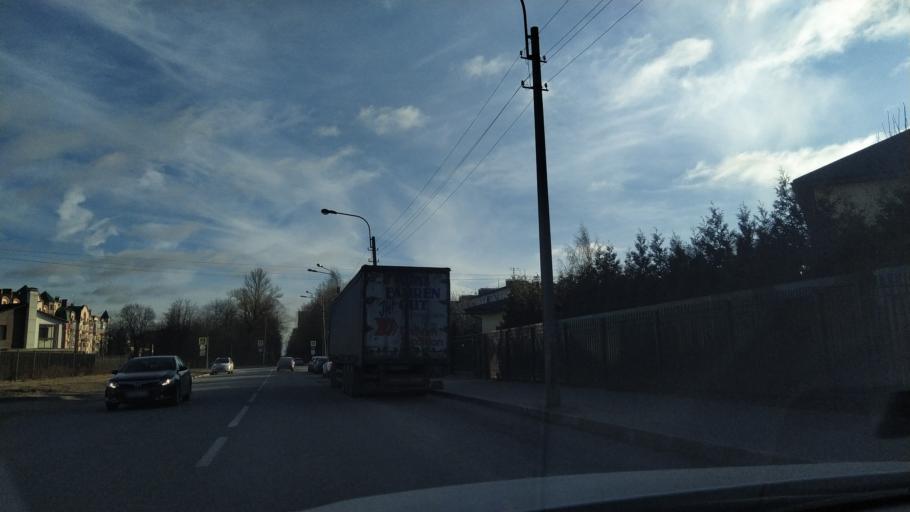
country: RU
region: St.-Petersburg
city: Pushkin
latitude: 59.7342
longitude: 30.4084
